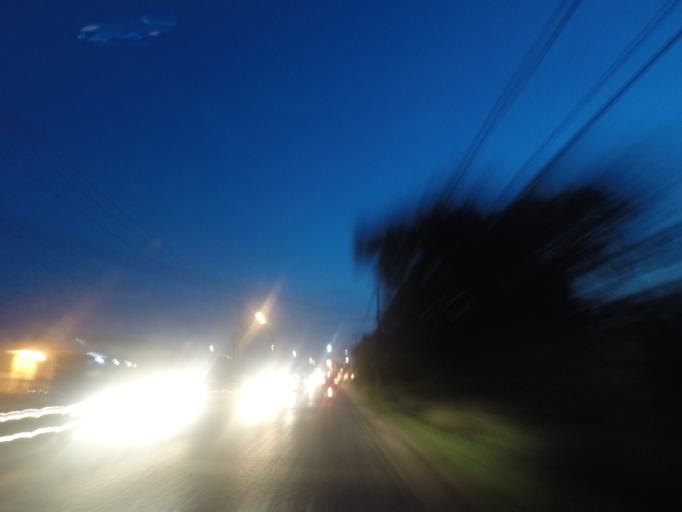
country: BR
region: Parana
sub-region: Pinhais
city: Pinhais
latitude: -25.4942
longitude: -49.1611
